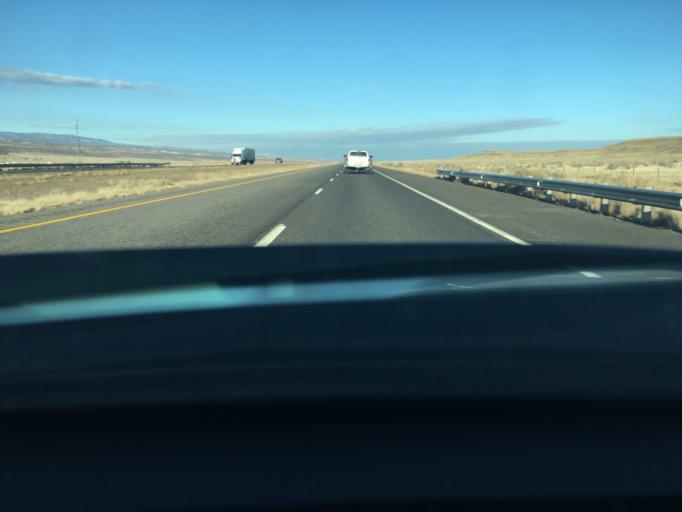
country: US
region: Colorado
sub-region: Mesa County
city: Palisade
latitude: 38.8692
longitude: -108.3337
